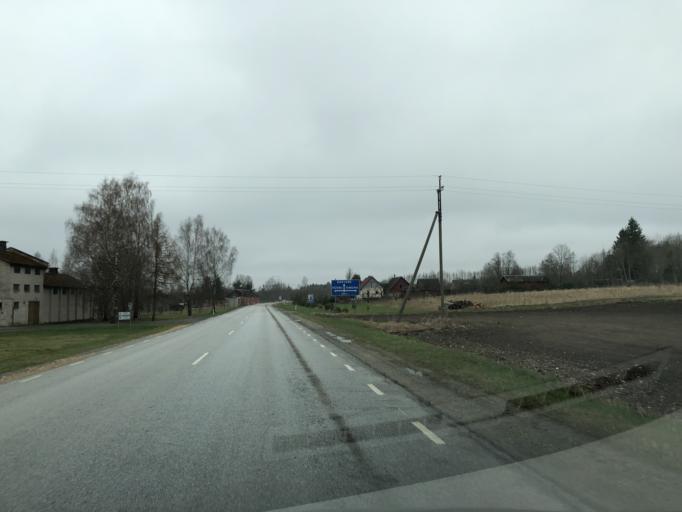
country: EE
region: Laeaene-Virumaa
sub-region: Rakke vald
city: Rakke
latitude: 58.9827
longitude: 26.2644
